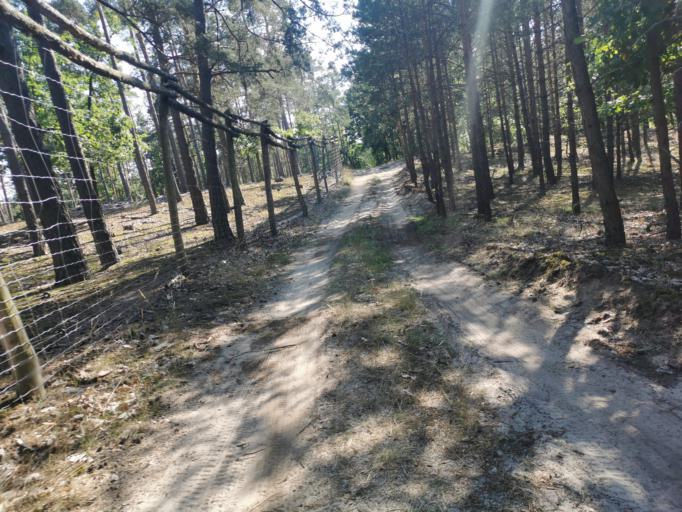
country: SK
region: Trnavsky
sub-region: Okres Senica
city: Senica
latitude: 48.6162
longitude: 17.2782
